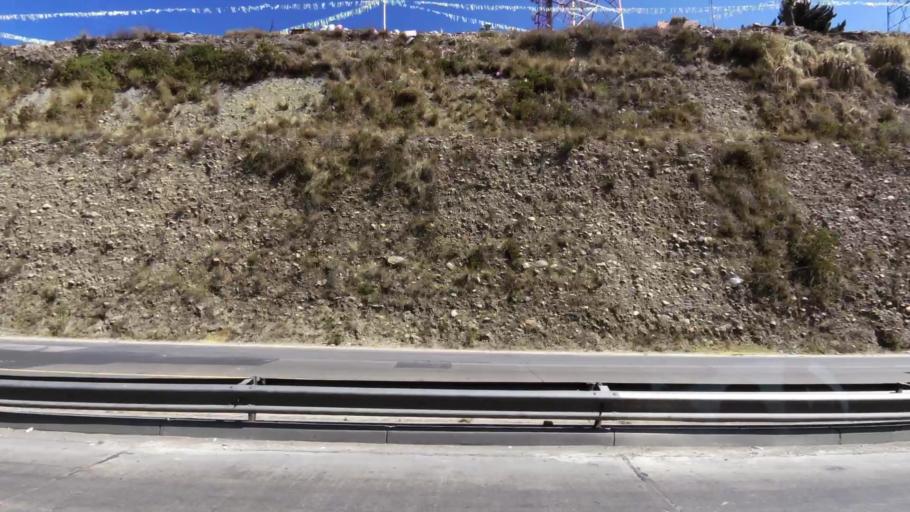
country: BO
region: La Paz
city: La Paz
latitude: -16.4987
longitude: -68.1632
